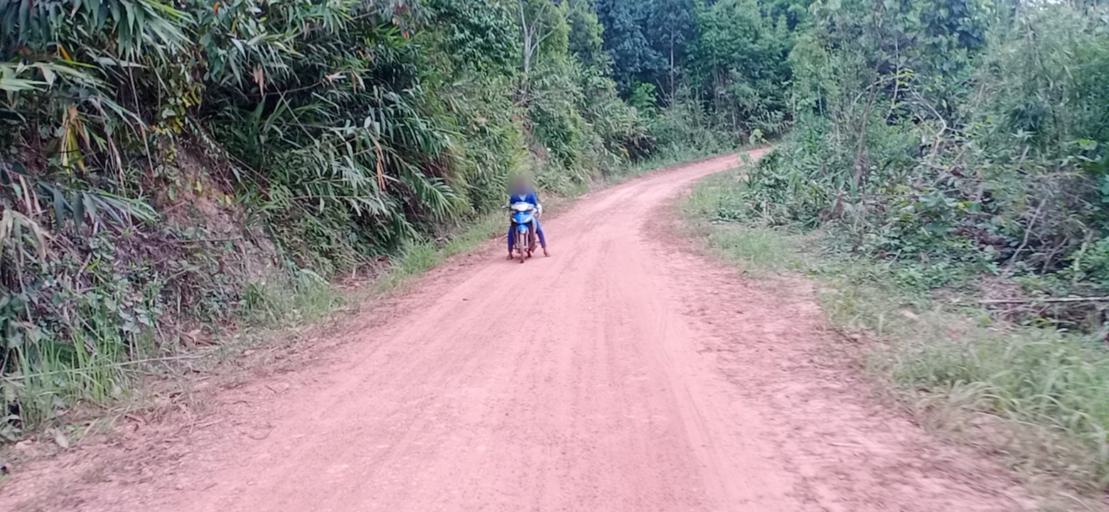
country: TH
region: Changwat Bueng Kan
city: Pak Khat
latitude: 18.5545
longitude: 103.1751
